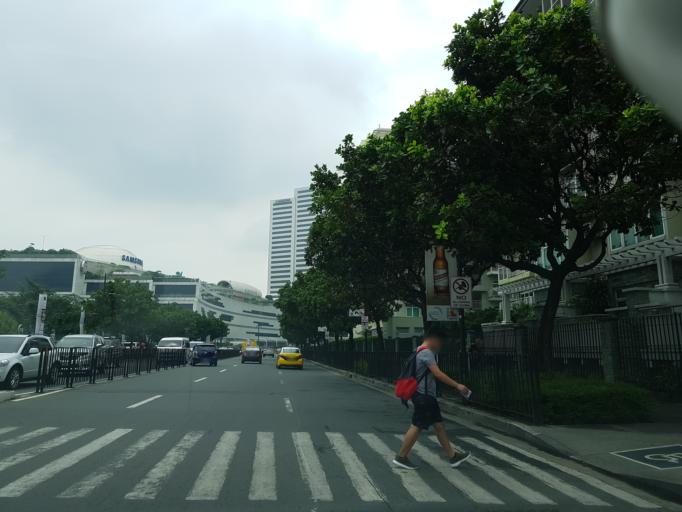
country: PH
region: Calabarzon
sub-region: Province of Rizal
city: Pateros
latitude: 14.5489
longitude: 121.0547
